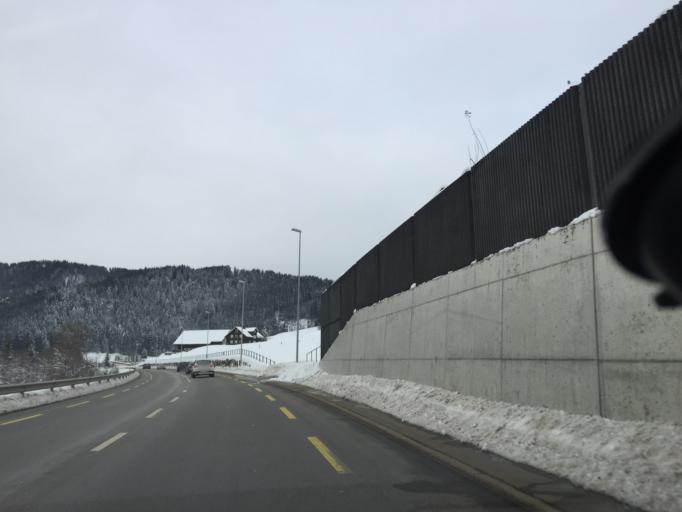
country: CH
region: Schwyz
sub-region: Bezirk Hoefe
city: Schindellegi
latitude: 47.1518
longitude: 8.7307
